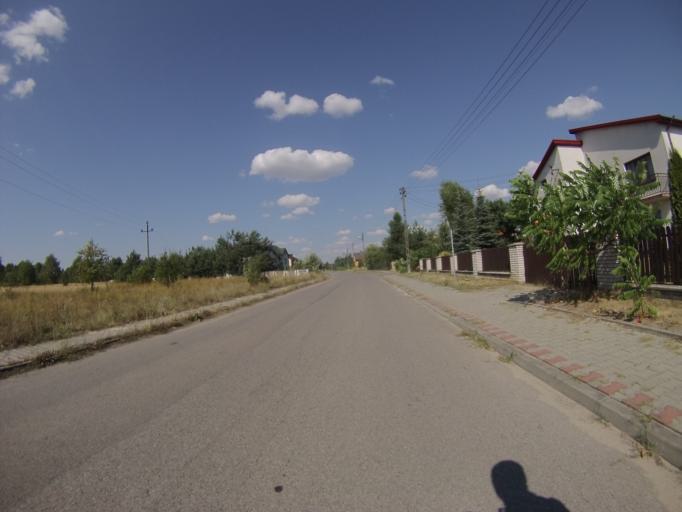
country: PL
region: Swietokrzyskie
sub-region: Powiat kielecki
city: Rakow
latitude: 50.6786
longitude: 21.0354
